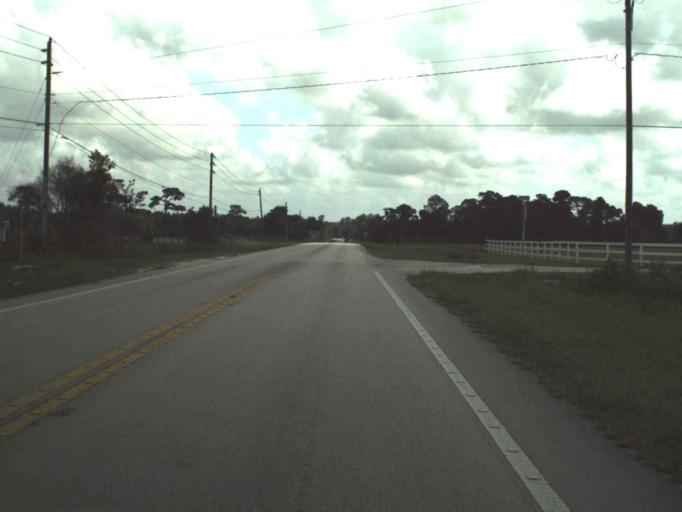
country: US
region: Florida
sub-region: Volusia County
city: Samsula-Spruce Creek
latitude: 28.9760
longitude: -81.0790
